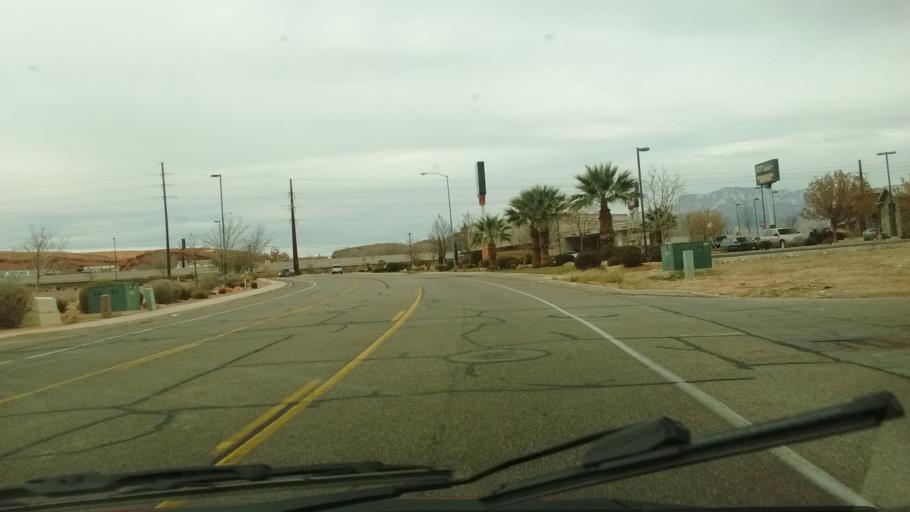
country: US
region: Utah
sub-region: Washington County
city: Washington
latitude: 37.1243
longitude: -113.5281
